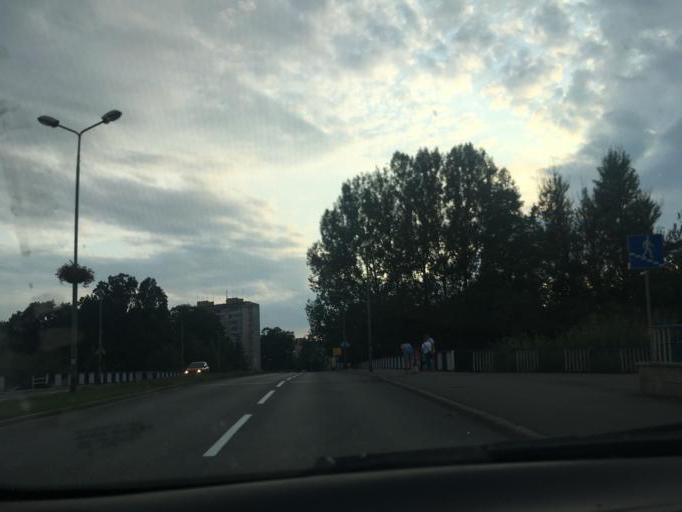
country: PL
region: Lower Silesian Voivodeship
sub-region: Powiat klodzki
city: Klodzko
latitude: 50.4366
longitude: 16.6572
